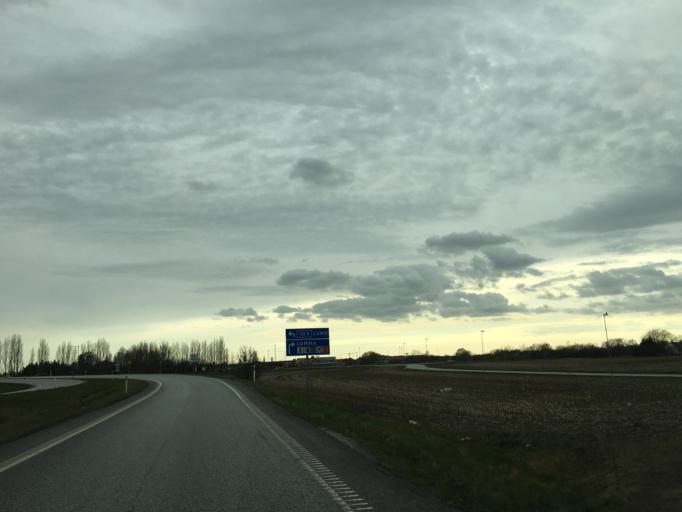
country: SE
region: Skane
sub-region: Lomma Kommun
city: Lomma
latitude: 55.6879
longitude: 13.0963
